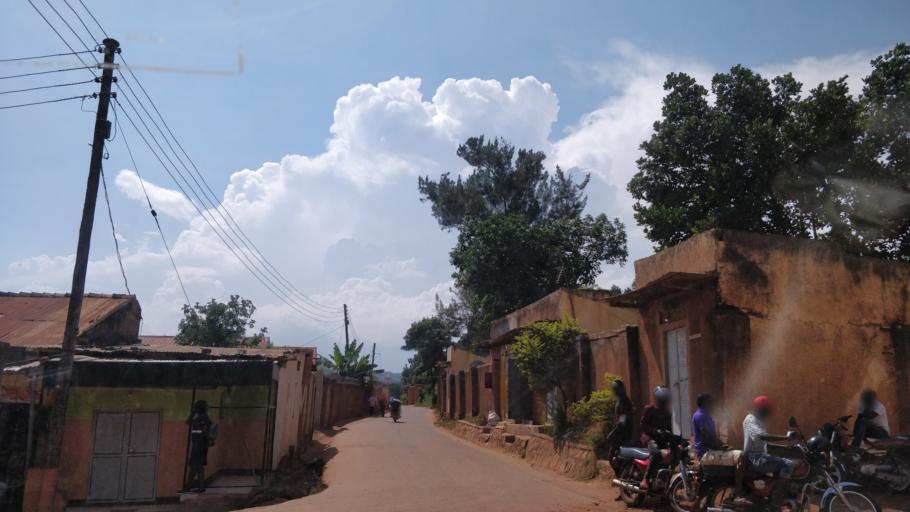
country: UG
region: Central Region
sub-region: Kampala District
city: Kampala
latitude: 0.2841
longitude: 32.6171
